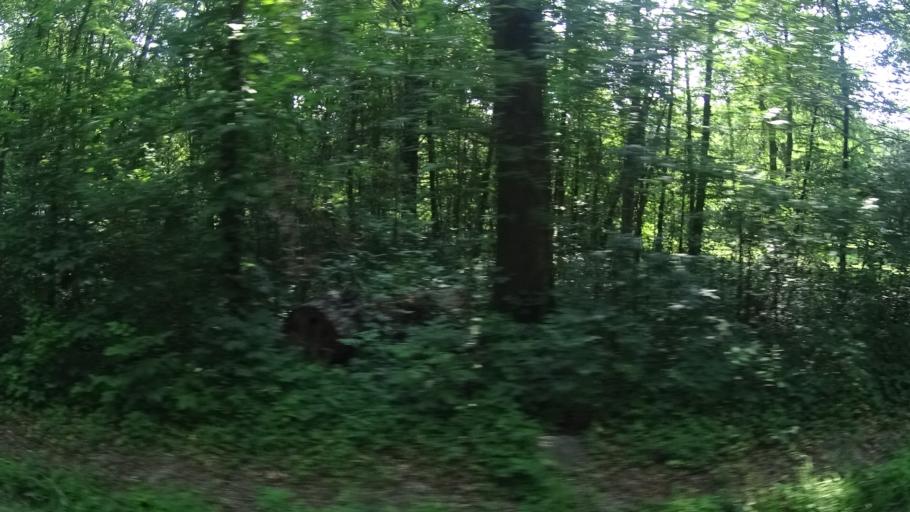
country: US
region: Ohio
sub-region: Lorain County
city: Vermilion
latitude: 41.3698
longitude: -82.4305
